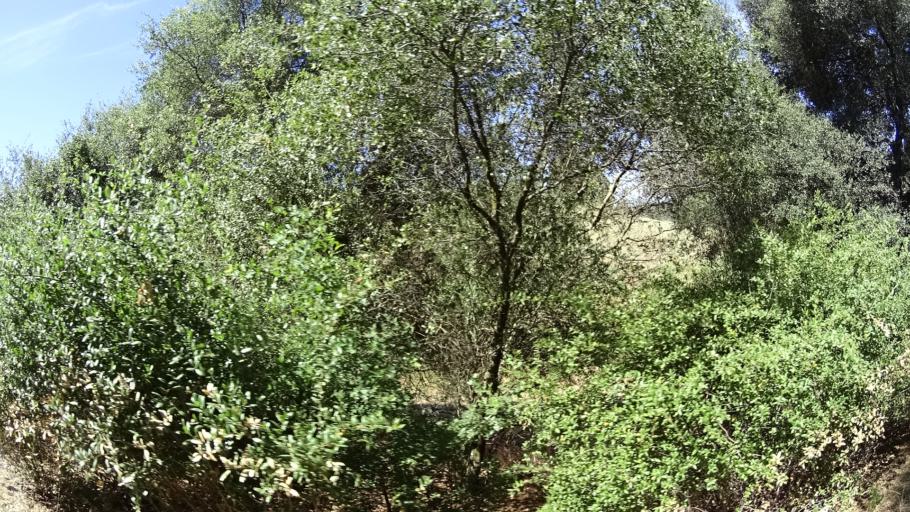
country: US
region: California
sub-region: Calaveras County
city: Angels Camp
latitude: 38.1244
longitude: -120.5764
